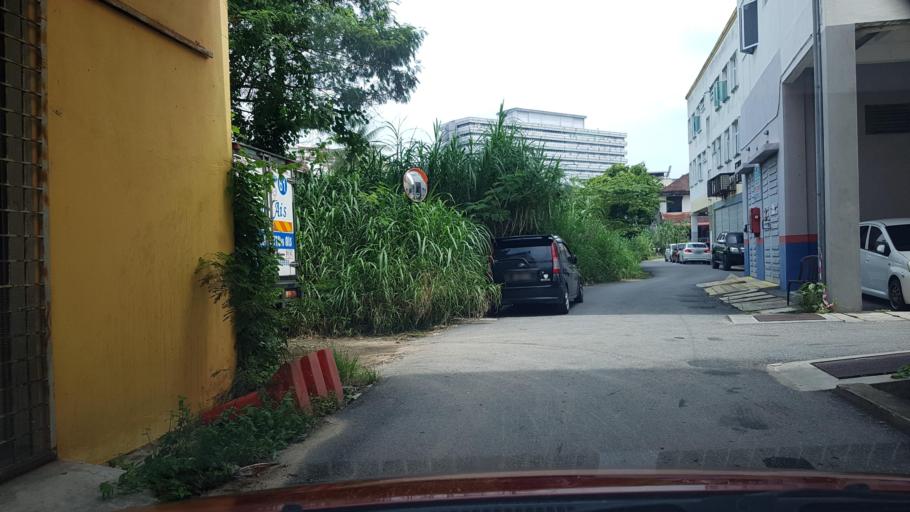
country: MY
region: Terengganu
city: Kuala Terengganu
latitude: 5.3314
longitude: 103.1436
